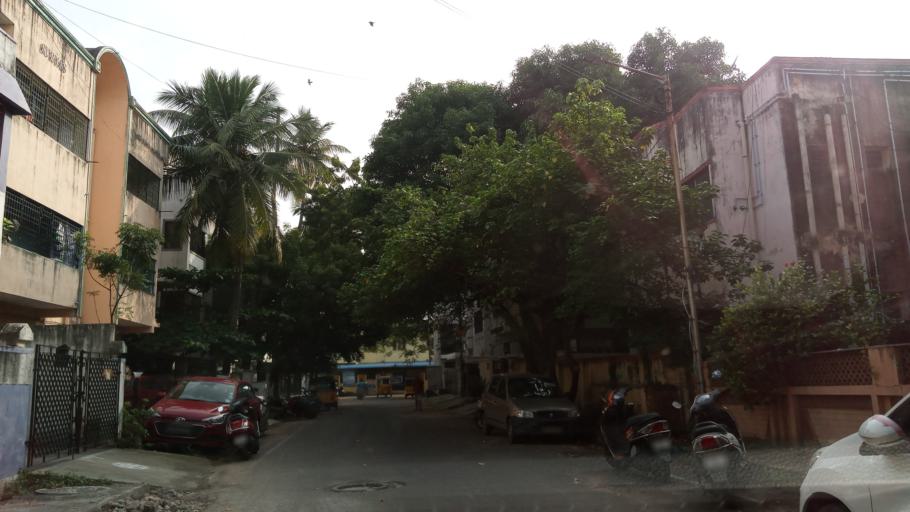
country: IN
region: Tamil Nadu
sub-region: Chennai
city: Chetput
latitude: 13.0400
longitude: 80.2234
